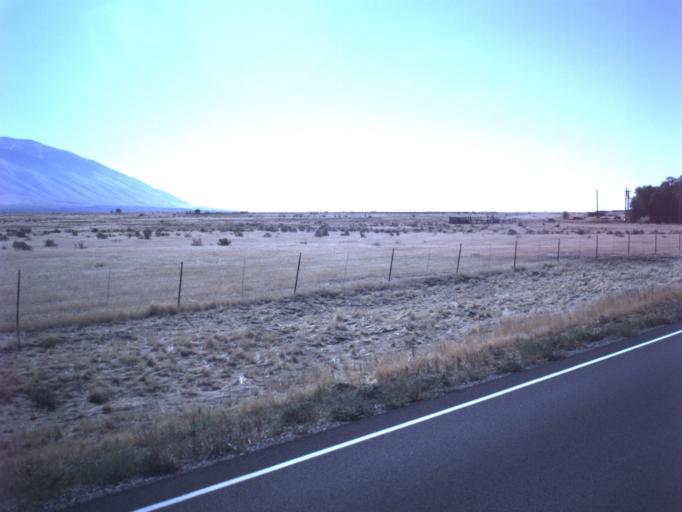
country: US
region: Utah
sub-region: Tooele County
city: Grantsville
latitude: 40.5401
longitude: -112.7456
